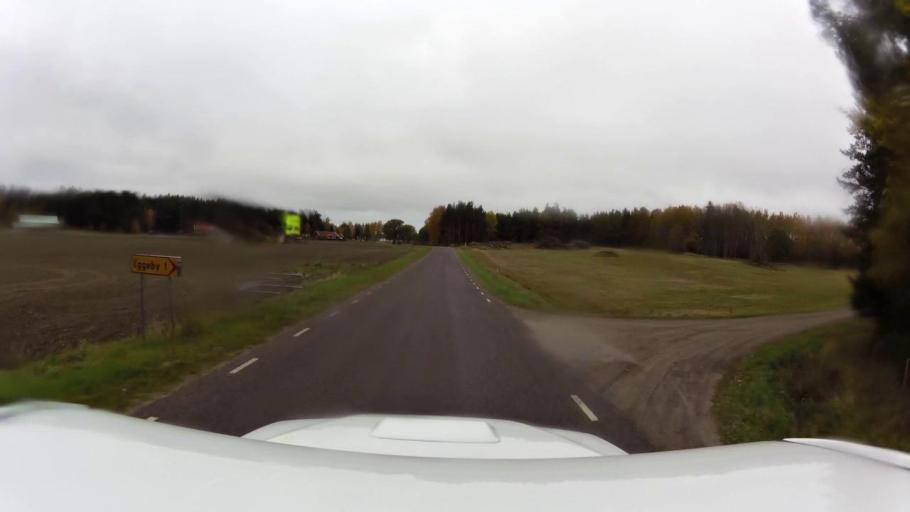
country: SE
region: OEstergoetland
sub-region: Linkopings Kommun
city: Linghem
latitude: 58.4675
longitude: 15.7681
